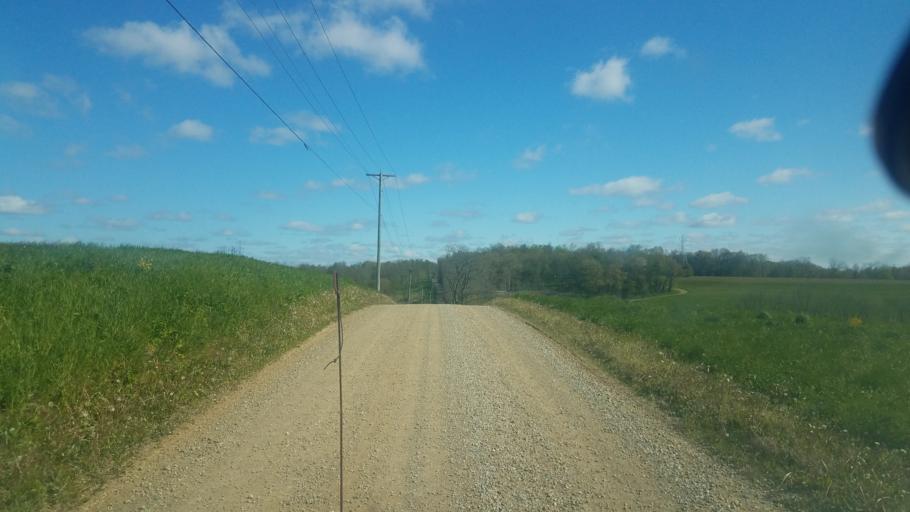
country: US
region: Ohio
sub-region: Knox County
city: Danville
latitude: 40.4259
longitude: -82.3226
